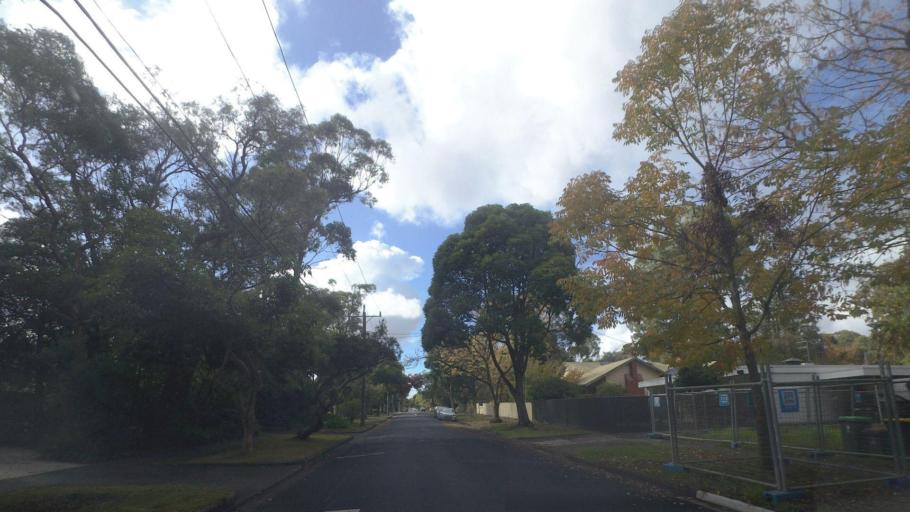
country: AU
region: Victoria
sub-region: Whitehorse
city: Blackburn
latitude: -37.8222
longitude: 145.1454
